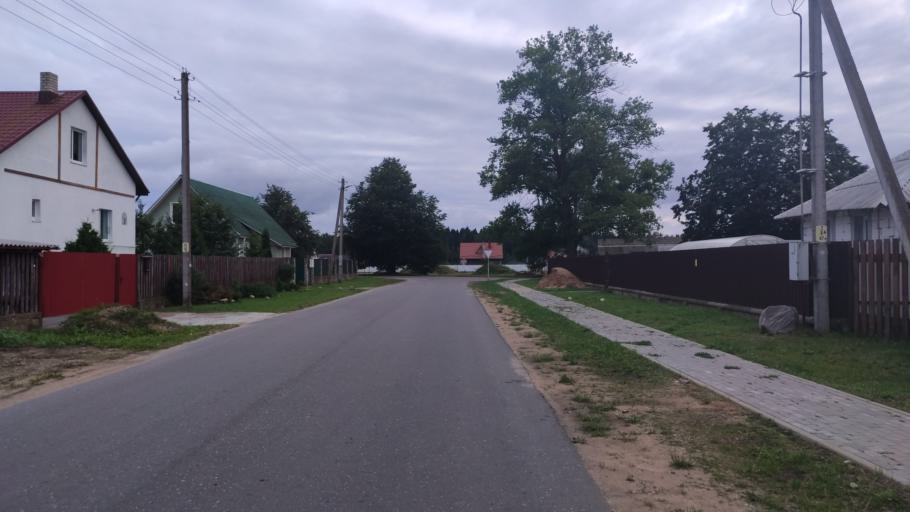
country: BY
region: Minsk
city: Narach
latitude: 54.9253
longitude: 26.6927
